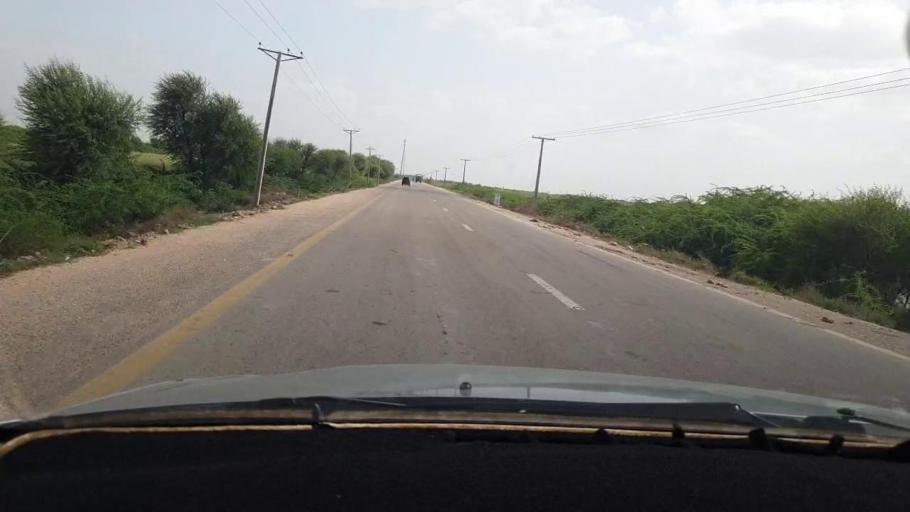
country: PK
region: Sindh
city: Naukot
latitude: 24.9202
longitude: 69.3214
